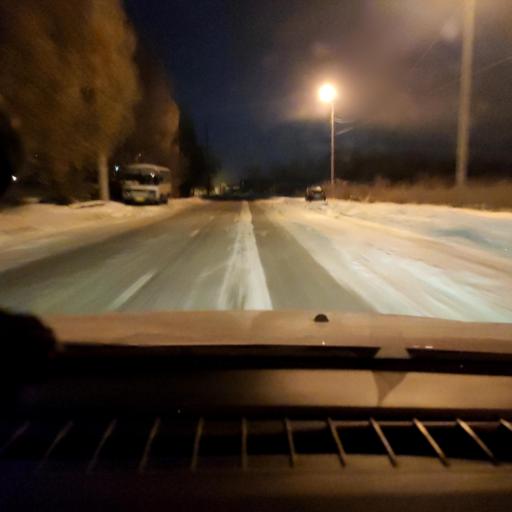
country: RU
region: Samara
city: Samara
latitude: 53.1414
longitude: 50.1454
